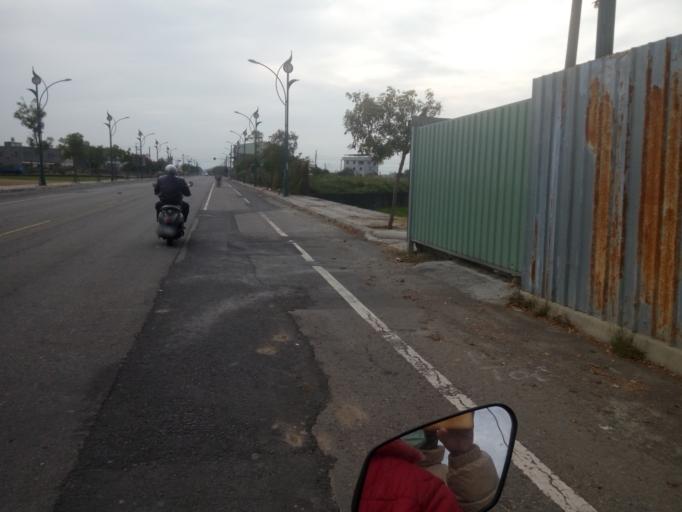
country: TW
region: Taiwan
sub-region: Chiayi
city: Taibao
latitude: 23.4963
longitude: 120.3612
